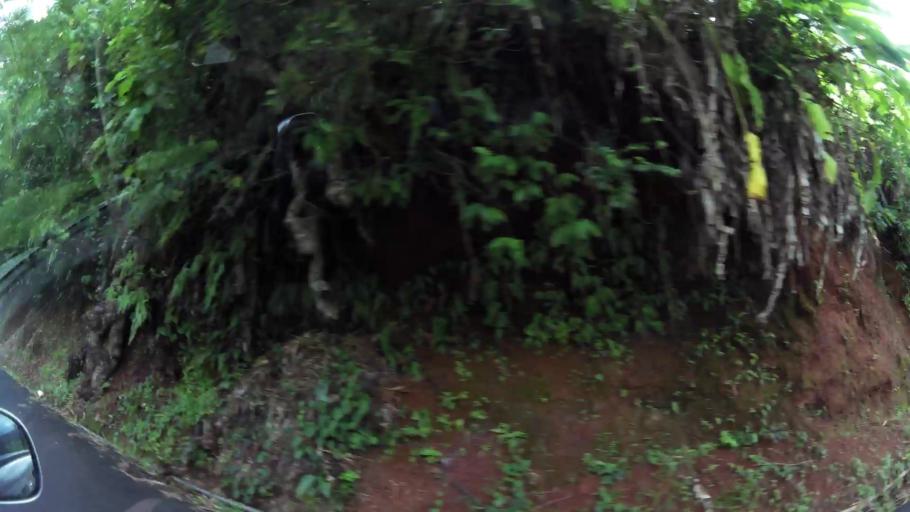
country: GD
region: Saint Andrew
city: Grenville
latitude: 12.1121
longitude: -61.6725
